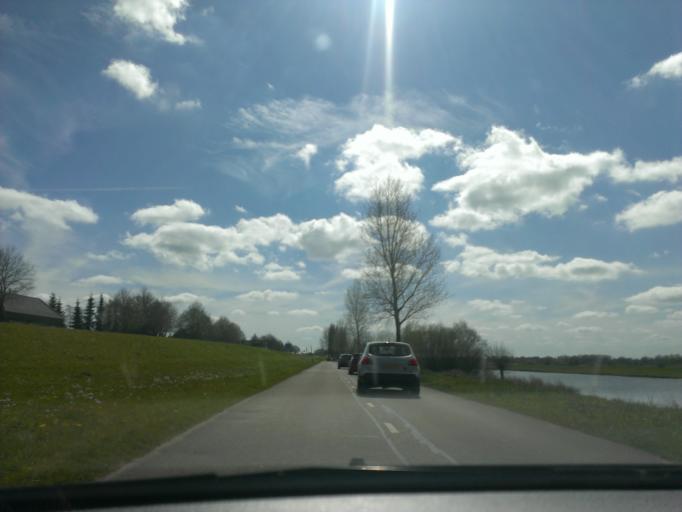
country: NL
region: Overijssel
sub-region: Gemeente Olst-Wijhe
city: Wijhe
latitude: 52.3901
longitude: 6.1287
